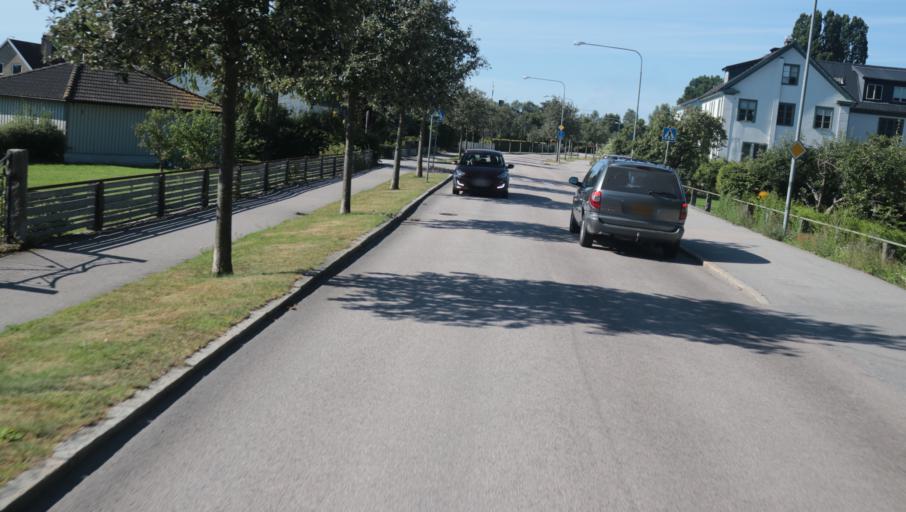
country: SE
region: Blekinge
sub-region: Karlshamns Kommun
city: Karlshamn
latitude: 56.2047
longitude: 14.8323
